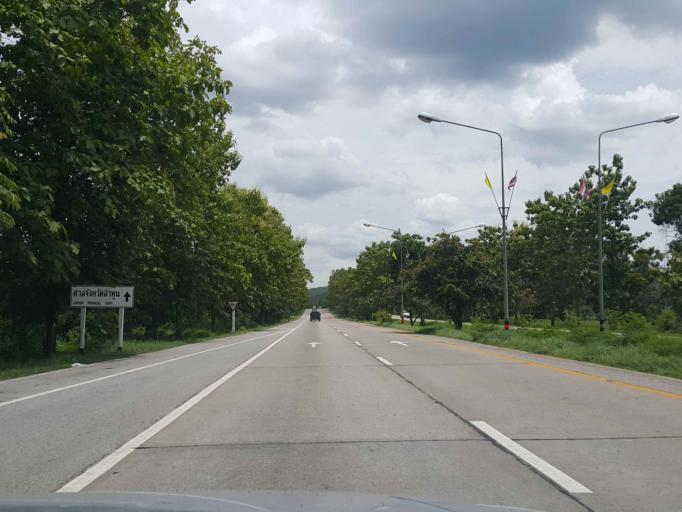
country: TH
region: Lamphun
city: Mae Tha
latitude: 18.5220
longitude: 99.0869
